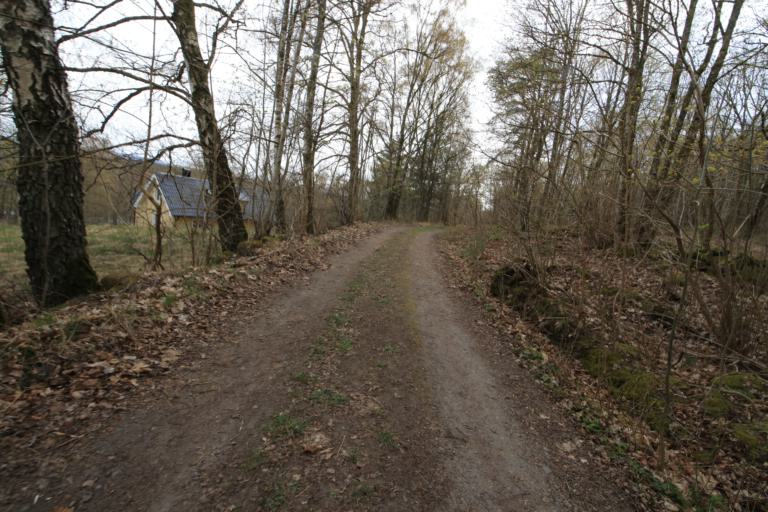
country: SE
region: Halland
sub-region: Varbergs Kommun
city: Tvaaker
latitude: 57.1518
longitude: 12.4628
